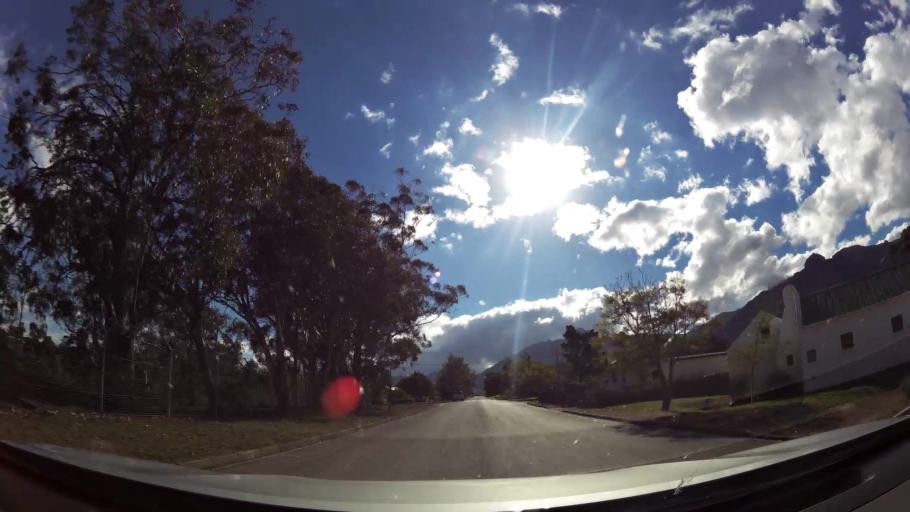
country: ZA
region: Western Cape
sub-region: Overberg District Municipality
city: Swellendam
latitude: -34.0198
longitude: 20.4386
